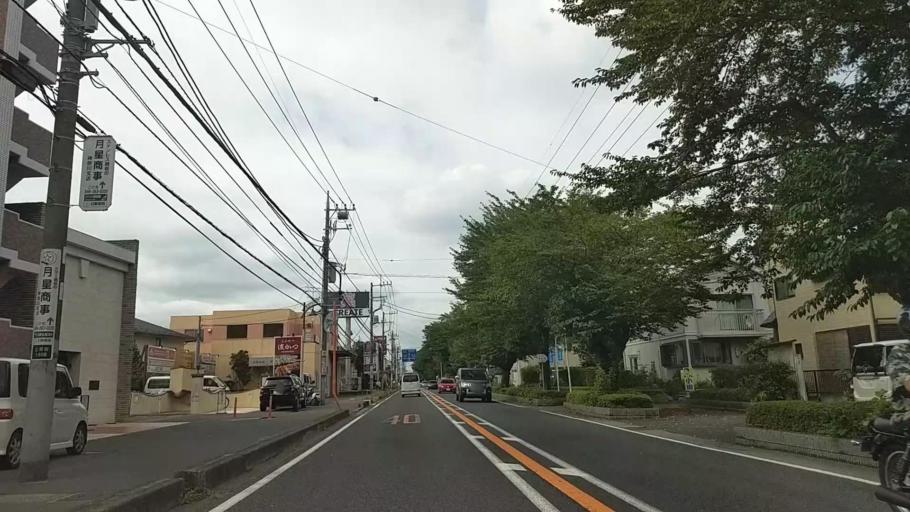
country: JP
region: Kanagawa
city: Minami-rinkan
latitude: 35.4450
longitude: 139.4673
